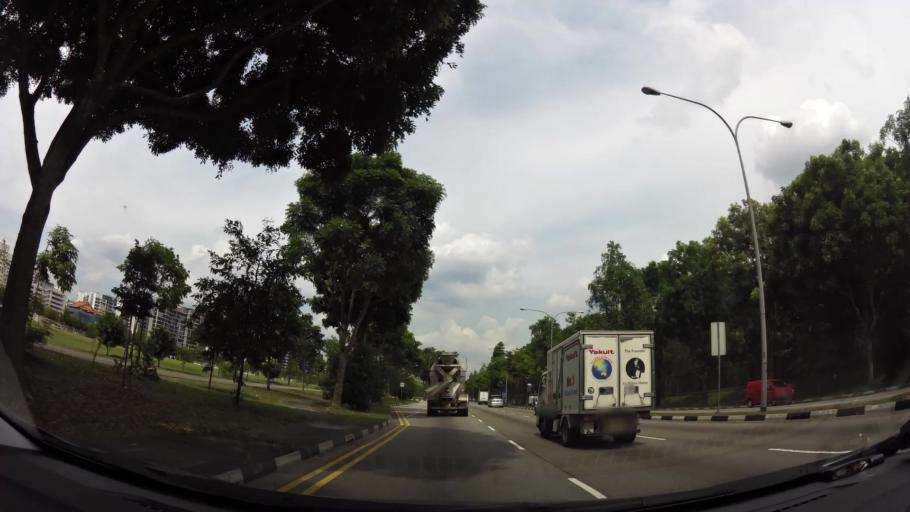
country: MY
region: Johor
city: Johor Bahru
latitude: 1.4275
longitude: 103.7992
